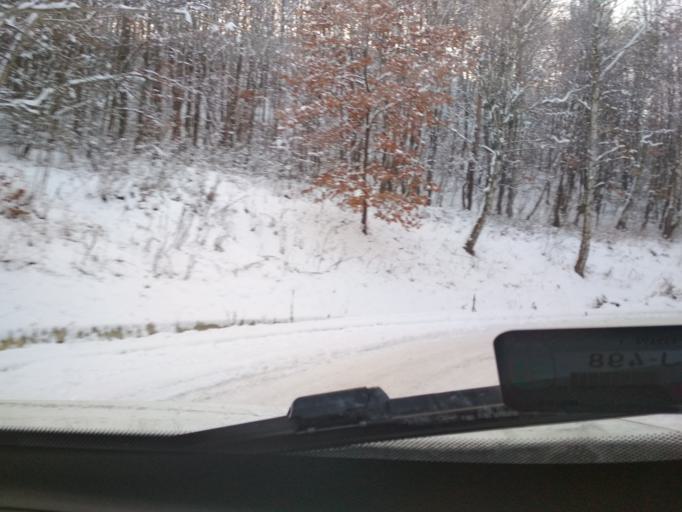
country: HU
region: Nograd
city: Somoskoujfalu
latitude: 48.1302
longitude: 19.8168
